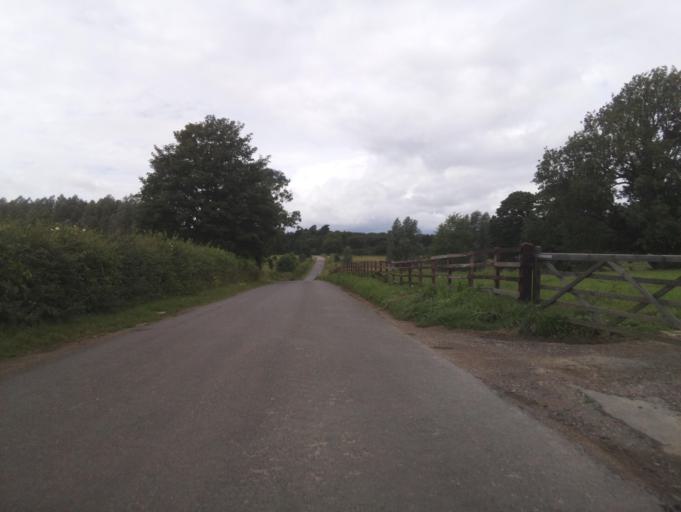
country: GB
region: England
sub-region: District of Rutland
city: Morcott
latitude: 52.5246
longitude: -0.5920
